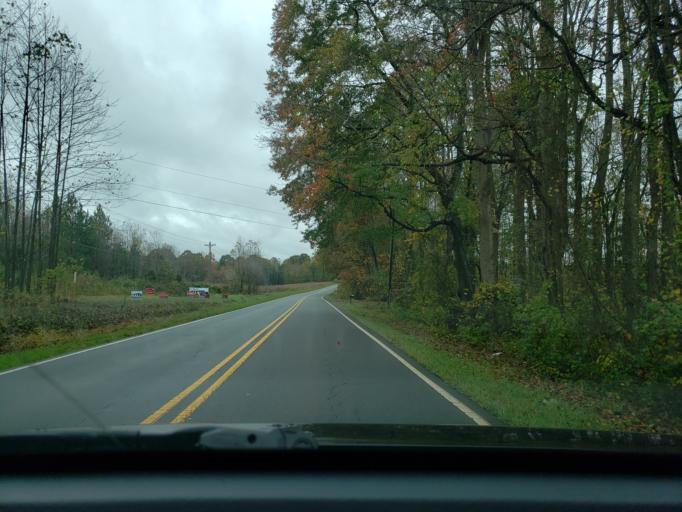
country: US
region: North Carolina
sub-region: Stokes County
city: Walnut Cove
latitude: 36.3471
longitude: -80.1543
